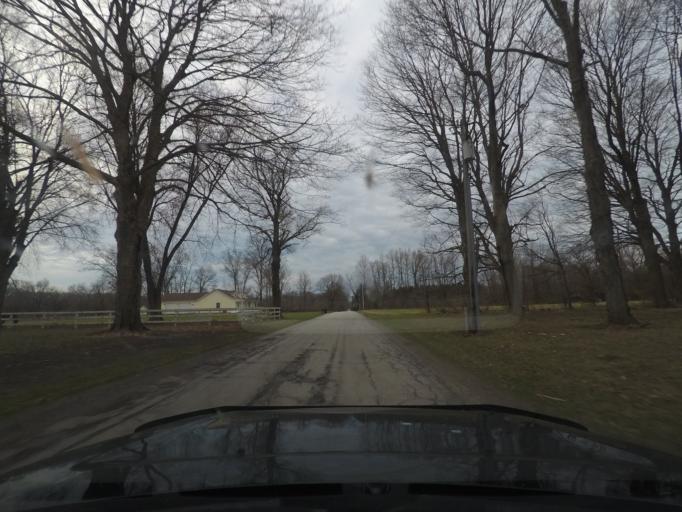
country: US
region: Indiana
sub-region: LaPorte County
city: Westville
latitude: 41.5262
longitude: -86.7988
